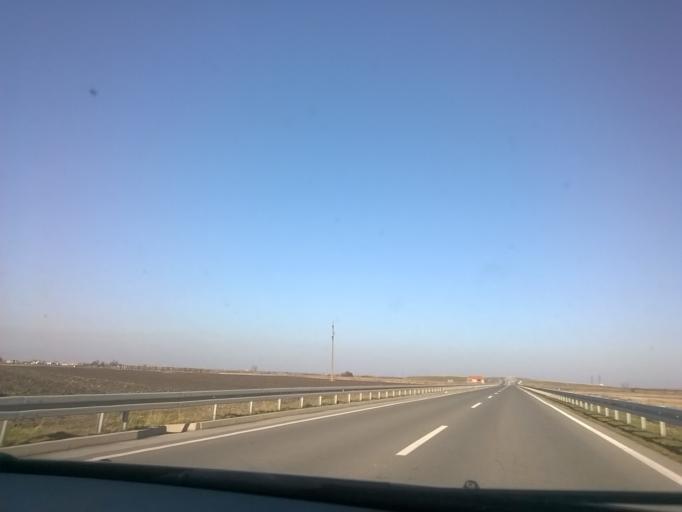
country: RS
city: Pavlis
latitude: 45.1043
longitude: 21.2613
